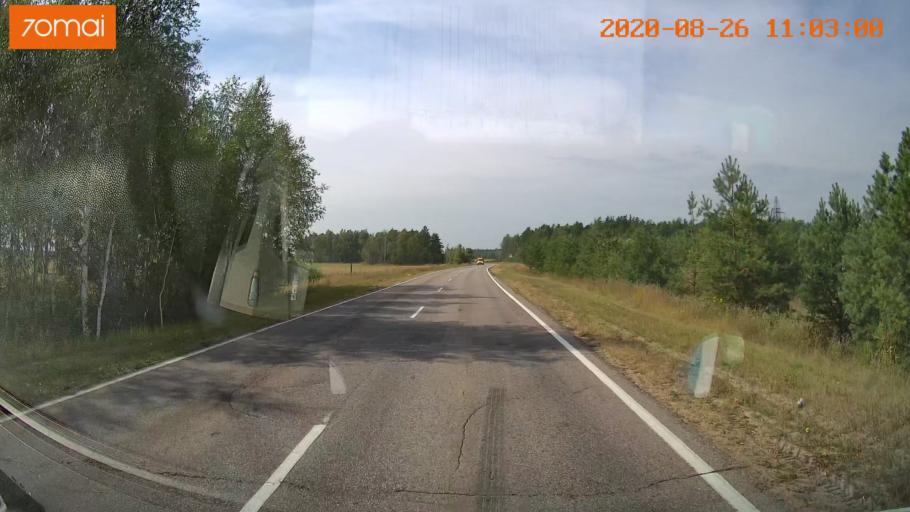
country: RU
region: Rjazan
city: Izhevskoye
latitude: 54.5443
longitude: 41.2190
